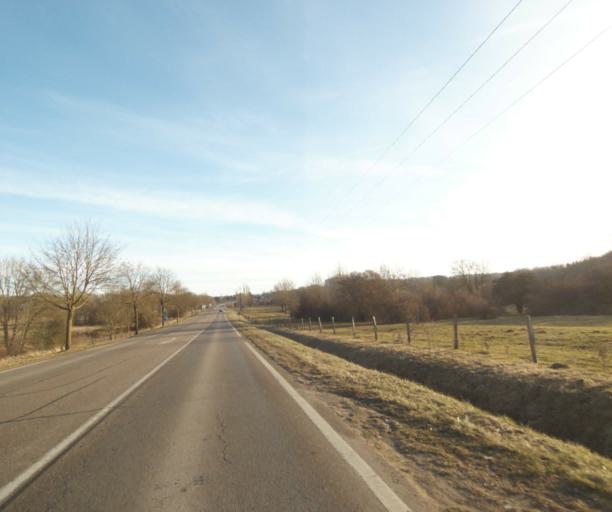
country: FR
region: Lorraine
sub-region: Departement de Meurthe-et-Moselle
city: Chavigny
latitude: 48.6397
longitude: 6.1322
